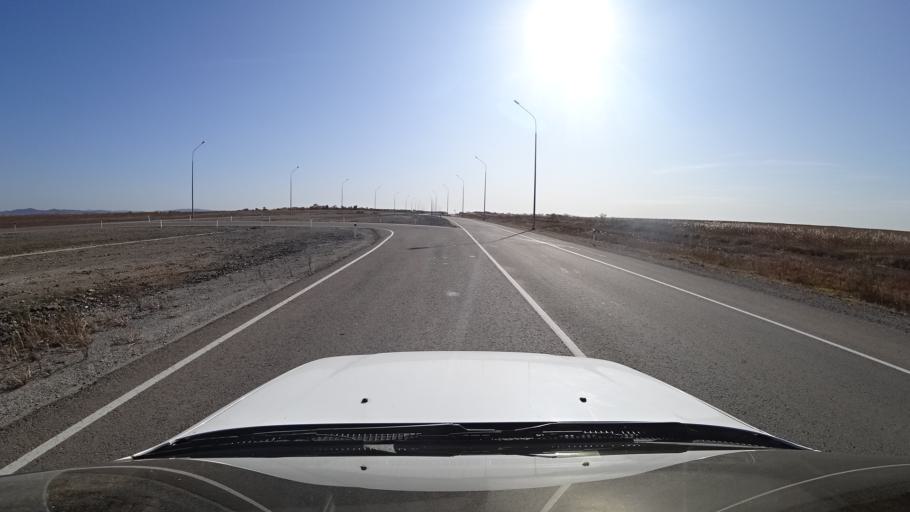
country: RU
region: Primorskiy
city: Lazo
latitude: 45.8635
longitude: 133.7197
